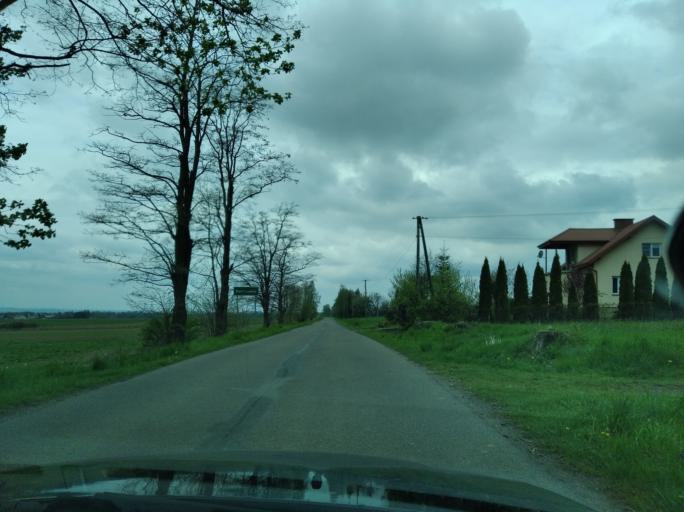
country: PL
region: Subcarpathian Voivodeship
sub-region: Powiat brzozowski
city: Gorki
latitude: 49.6117
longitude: 22.0441
